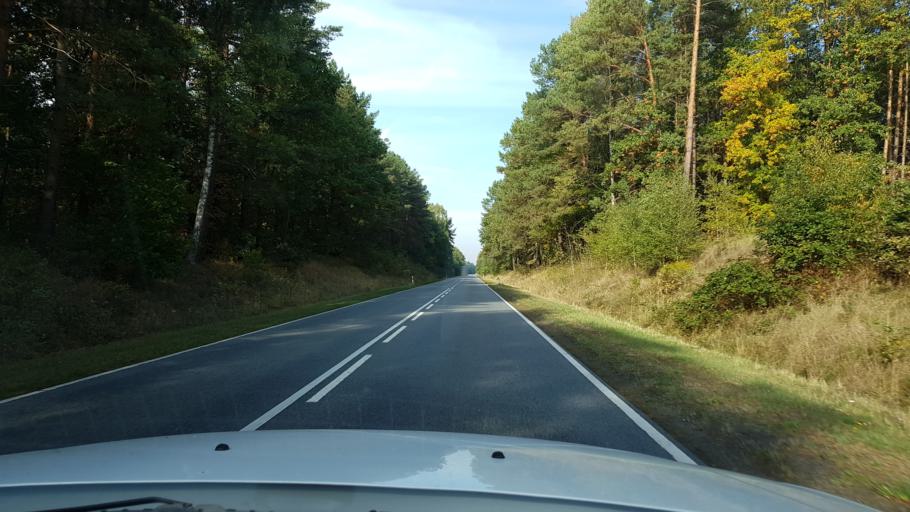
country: PL
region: West Pomeranian Voivodeship
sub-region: Powiat mysliborski
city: Nowogrodek Pomorski
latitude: 52.9194
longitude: 14.9654
